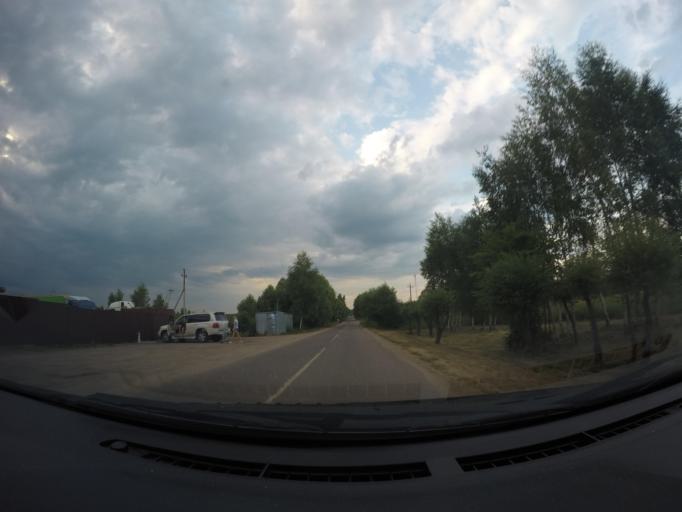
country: RU
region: Moskovskaya
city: Krasnyy Tkach
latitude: 55.4247
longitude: 39.2432
